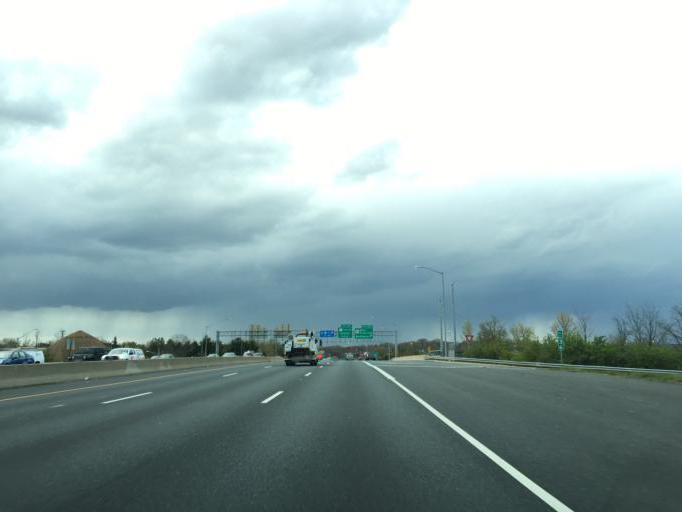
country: US
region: Maryland
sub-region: Baltimore County
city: Rossville
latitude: 39.3314
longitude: -76.4868
